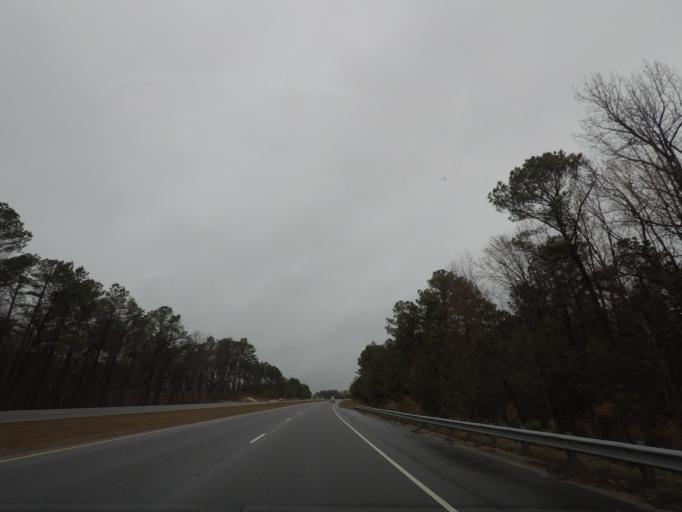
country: US
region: North Carolina
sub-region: Lee County
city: Broadway
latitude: 35.3283
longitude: -79.0937
